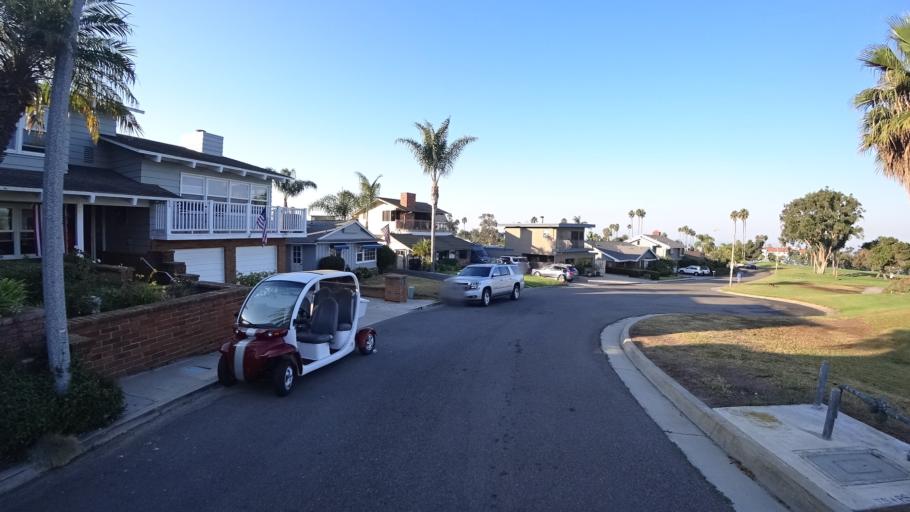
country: US
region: California
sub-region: Orange County
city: San Clemente
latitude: 33.4109
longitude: -117.5959
